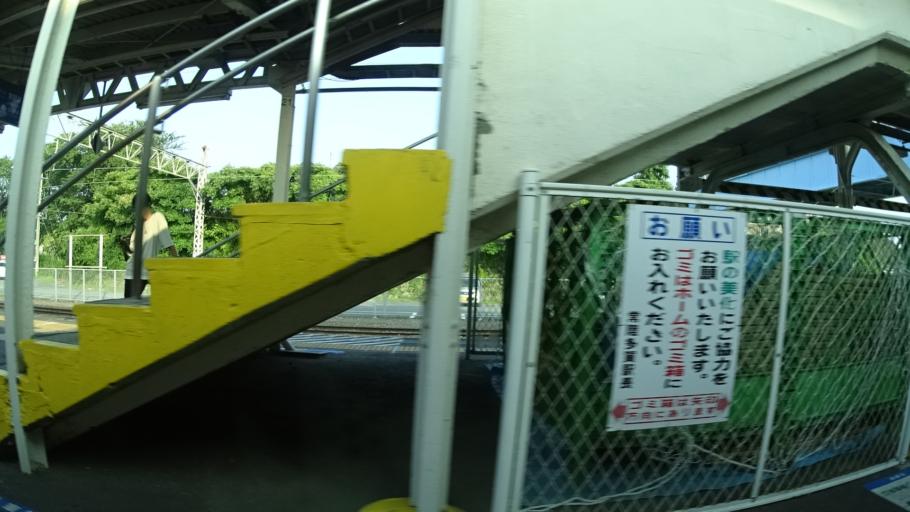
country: JP
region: Ibaraki
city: Hitachi
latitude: 36.5517
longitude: 140.6321
